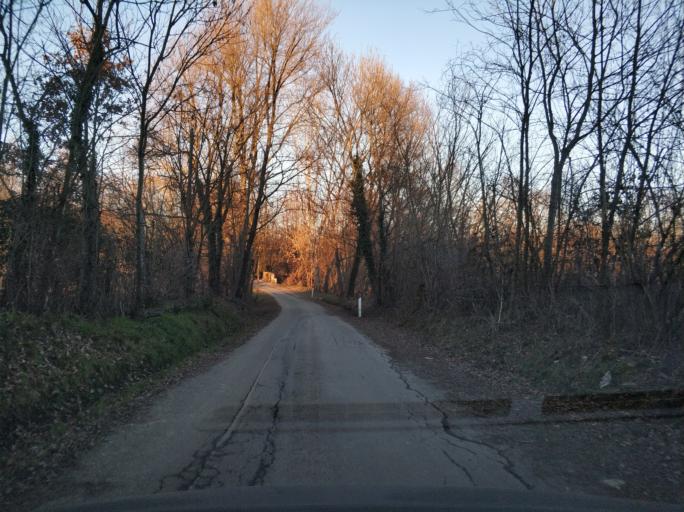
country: IT
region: Piedmont
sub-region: Provincia di Torino
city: San Francesco al Campo
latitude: 45.2440
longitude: 7.6378
